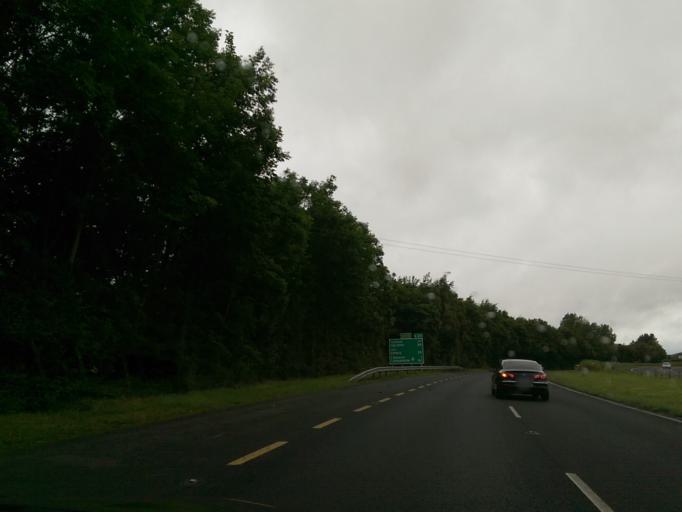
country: IE
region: Munster
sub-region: An Clar
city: Sixmilebridge
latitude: 52.6845
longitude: -8.7240
